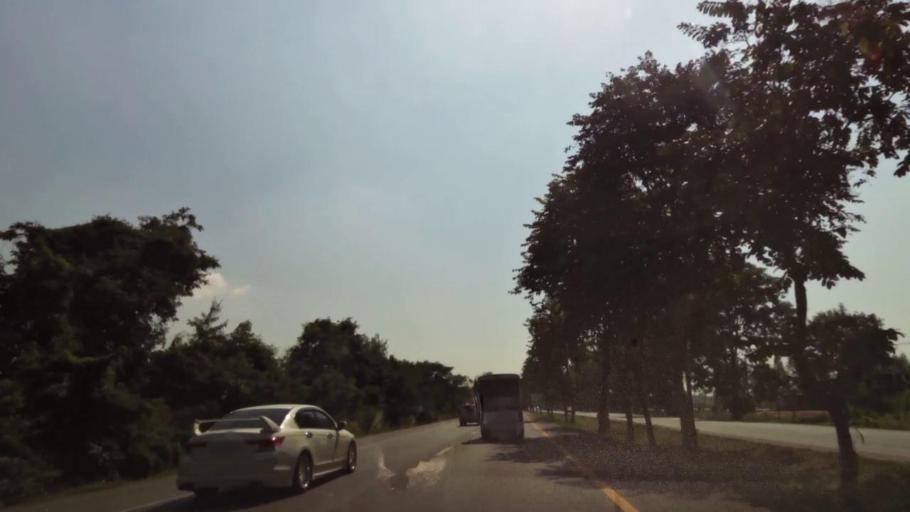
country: TH
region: Phichit
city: Bueng Na Rang
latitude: 16.1119
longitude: 100.1258
